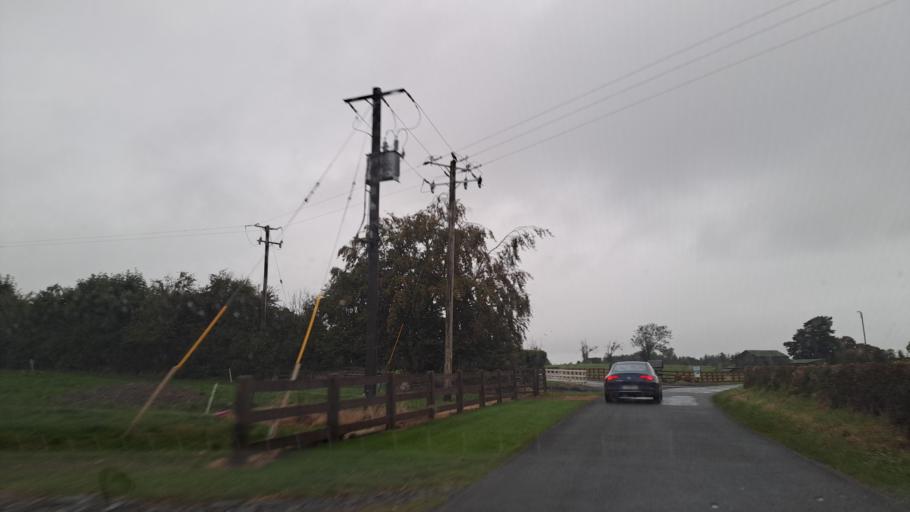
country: IE
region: Ulster
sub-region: County Monaghan
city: Monaghan
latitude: 54.2109
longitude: -6.9091
